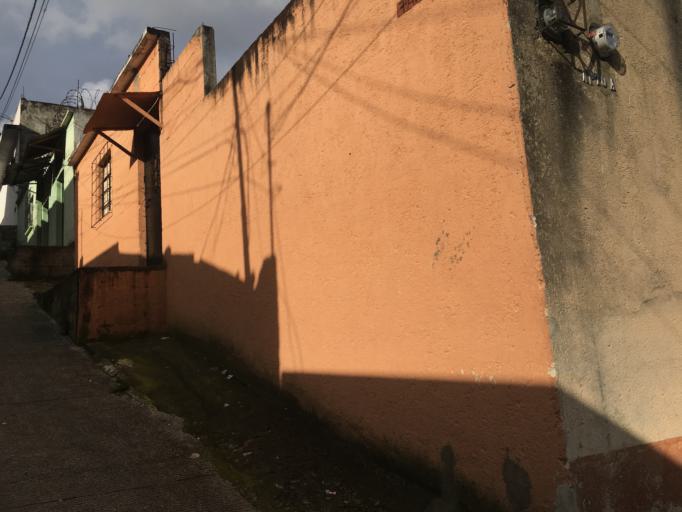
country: GT
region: Guatemala
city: Mixco
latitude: 14.6259
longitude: -90.5831
